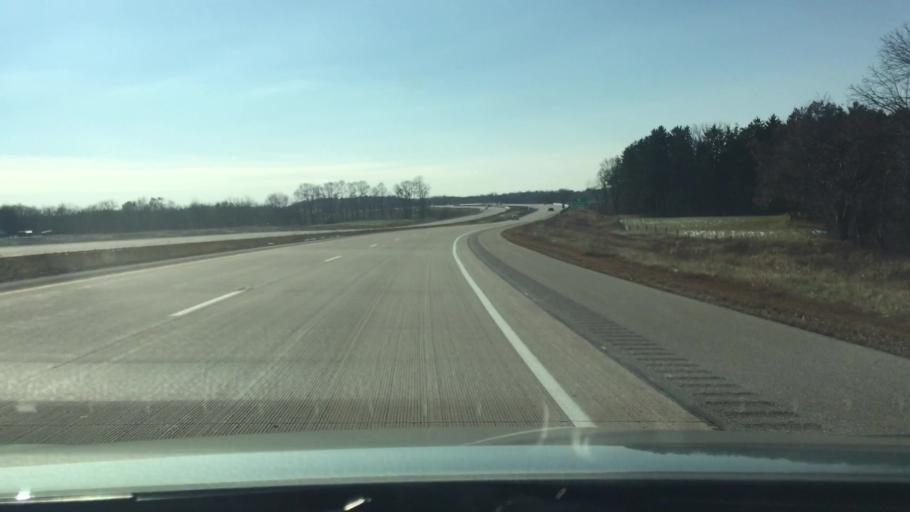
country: US
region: Wisconsin
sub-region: Jefferson County
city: Jefferson
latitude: 43.0131
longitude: -88.8295
